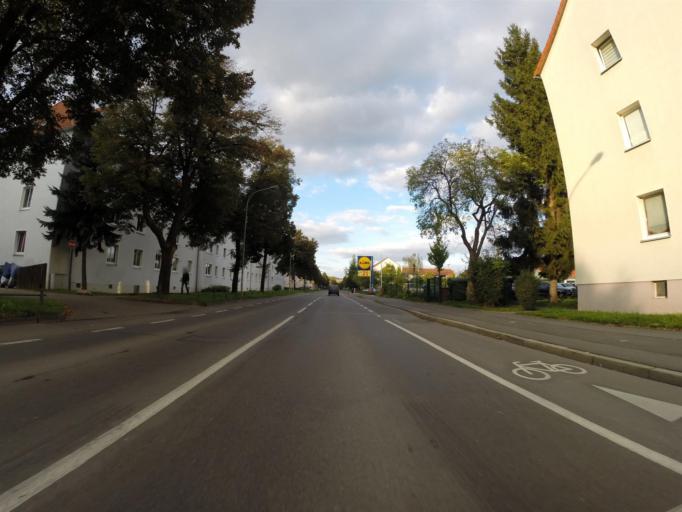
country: DE
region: Thuringia
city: Jena
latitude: 50.9377
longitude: 11.5910
